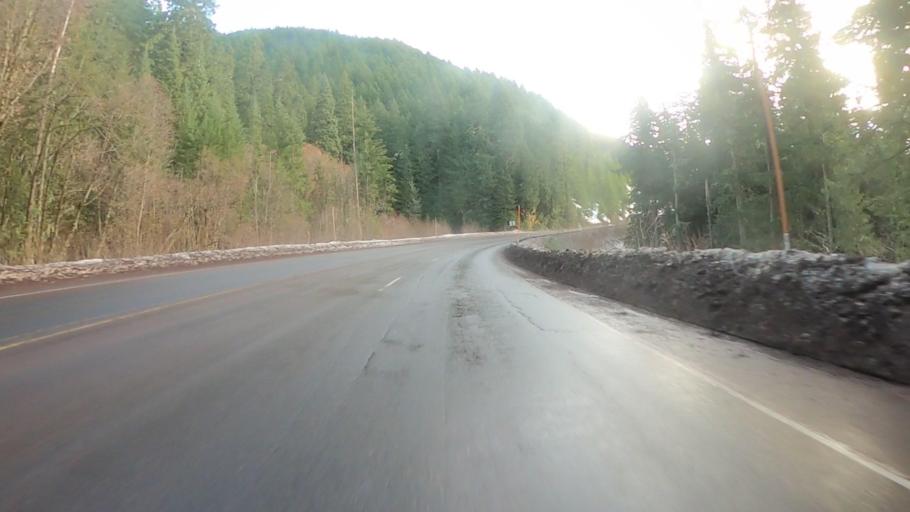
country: US
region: Oregon
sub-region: Lane County
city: Oakridge
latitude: 43.6267
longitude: -122.1418
